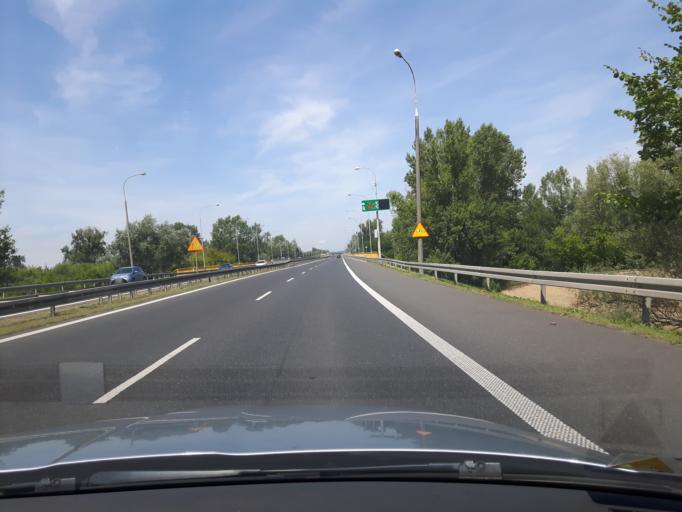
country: PL
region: Masovian Voivodeship
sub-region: Powiat nowodworski
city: Zakroczym
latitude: 52.4233
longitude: 20.6592
